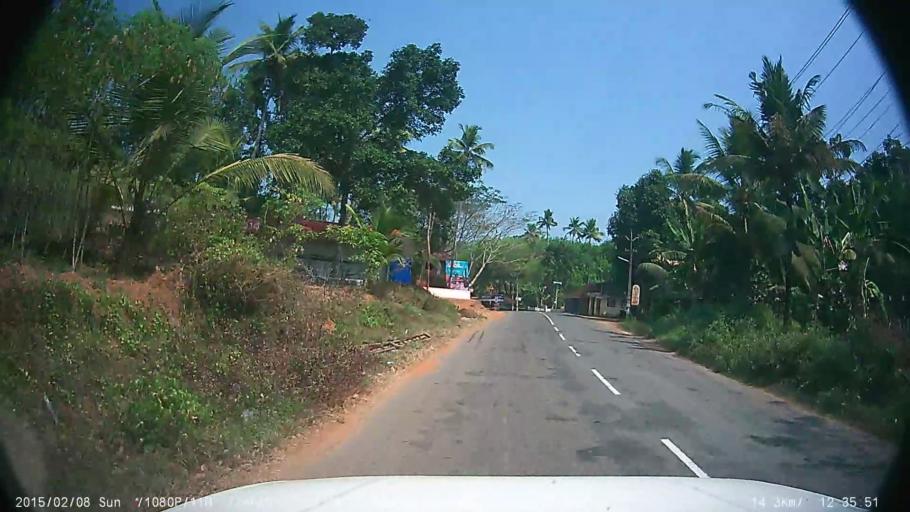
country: IN
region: Kerala
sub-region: Kottayam
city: Palackattumala
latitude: 9.7789
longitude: 76.5750
